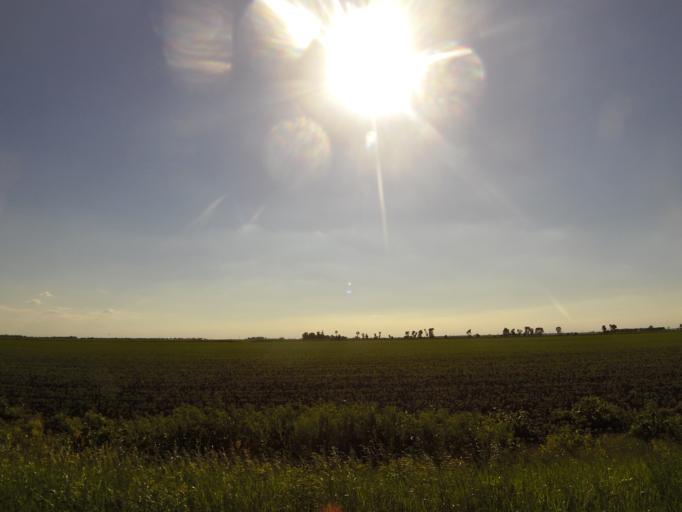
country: US
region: North Dakota
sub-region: Walsh County
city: Grafton
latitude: 48.4057
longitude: -97.2338
